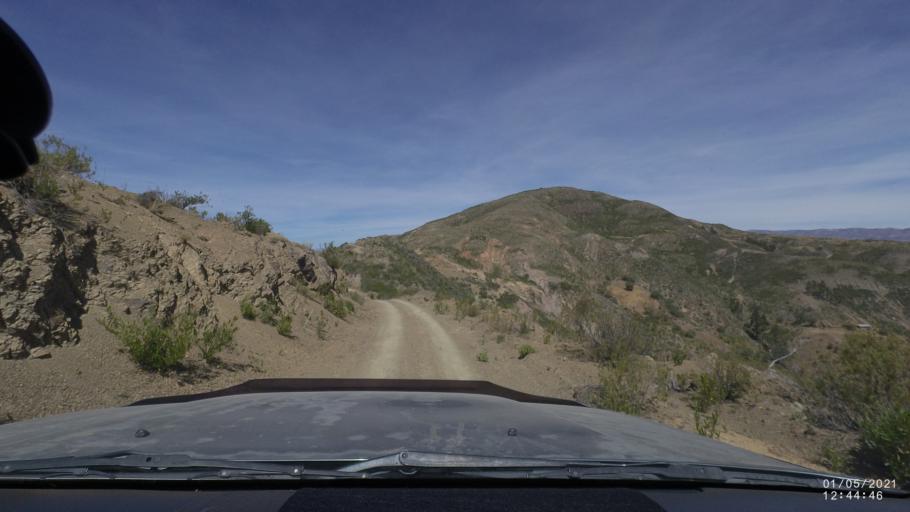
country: BO
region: Cochabamba
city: Capinota
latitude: -17.6844
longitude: -66.1603
